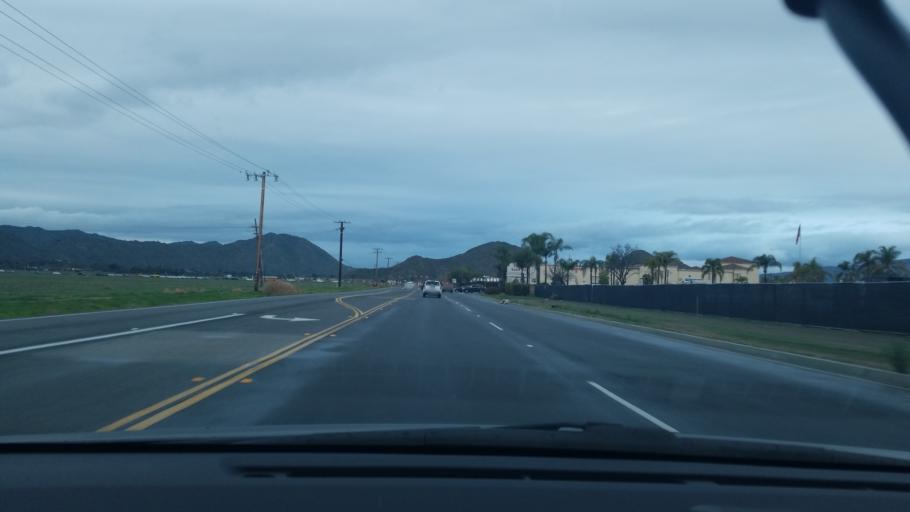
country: US
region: California
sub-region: Riverside County
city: Green Acres
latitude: 33.7391
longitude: -117.0327
